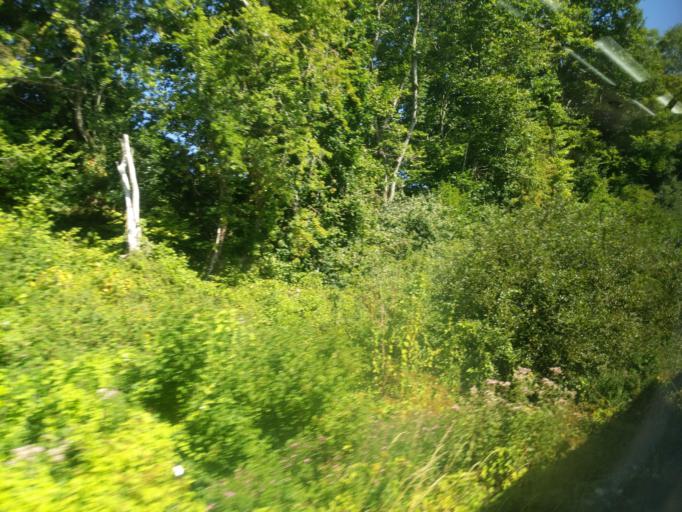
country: GB
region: England
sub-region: Devon
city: Kingskerswell
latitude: 50.4845
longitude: -3.5515
